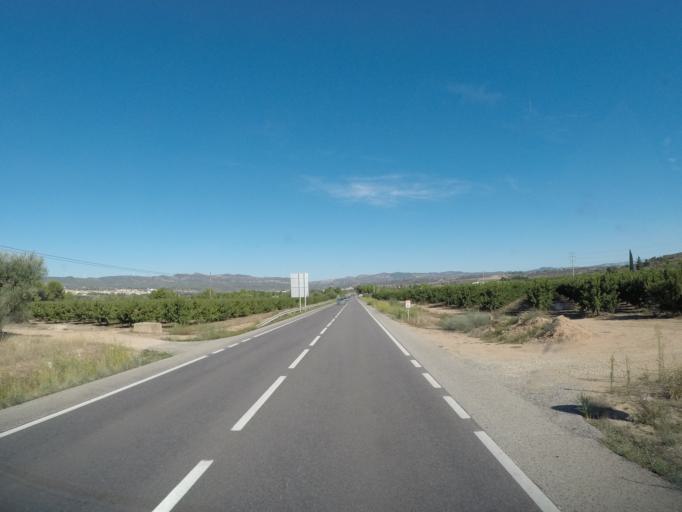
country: ES
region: Catalonia
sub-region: Provincia de Tarragona
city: Ginestar
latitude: 41.0743
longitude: 0.6631
